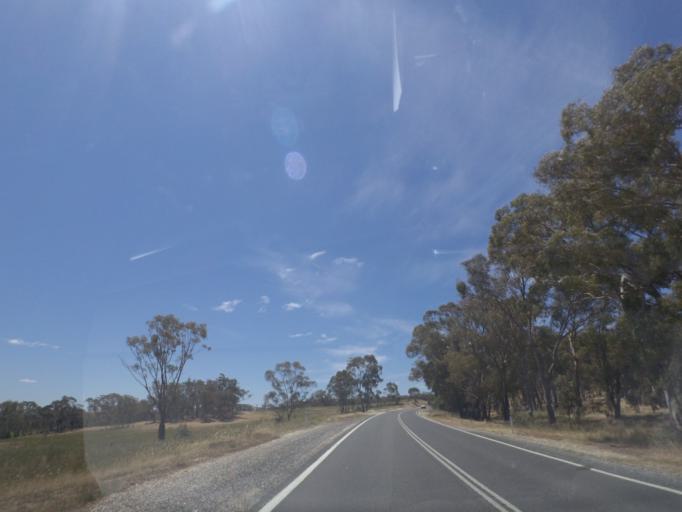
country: AU
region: Victoria
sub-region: Mount Alexander
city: Castlemaine
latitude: -37.1684
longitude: 144.1468
